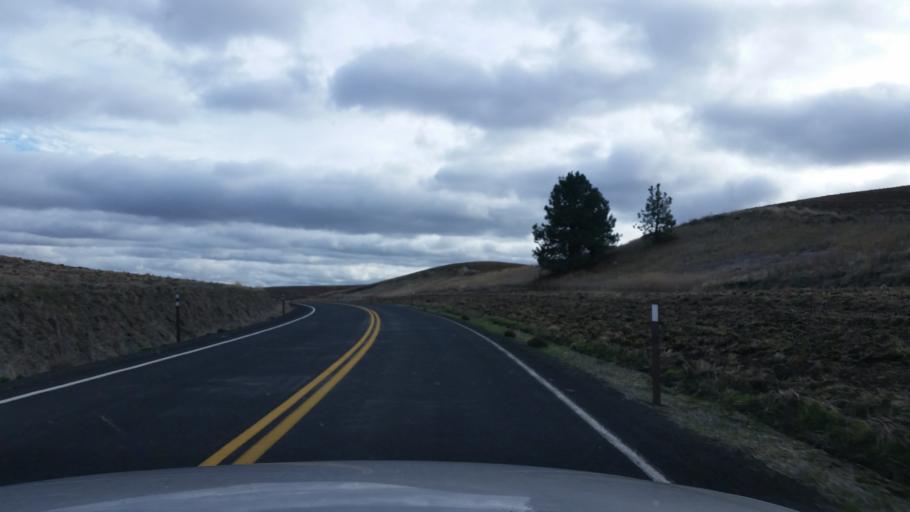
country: US
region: Washington
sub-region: Lincoln County
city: Davenport
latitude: 47.3467
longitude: -118.0207
